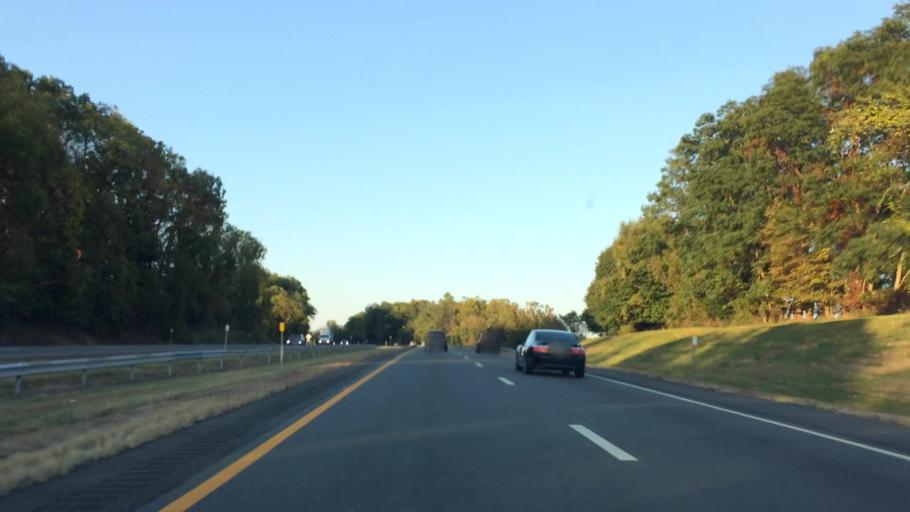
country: US
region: New York
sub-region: Orange County
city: Firthcliffe
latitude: 41.4126
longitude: -74.0731
